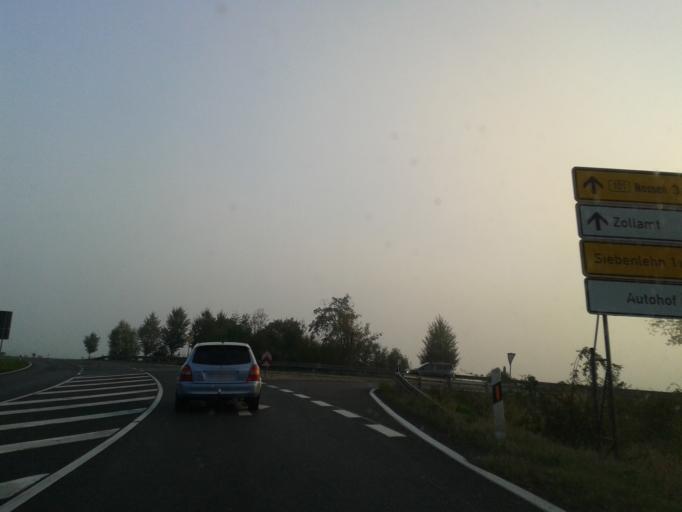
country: DE
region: Saxony
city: Nossen
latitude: 51.0381
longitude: 13.2964
